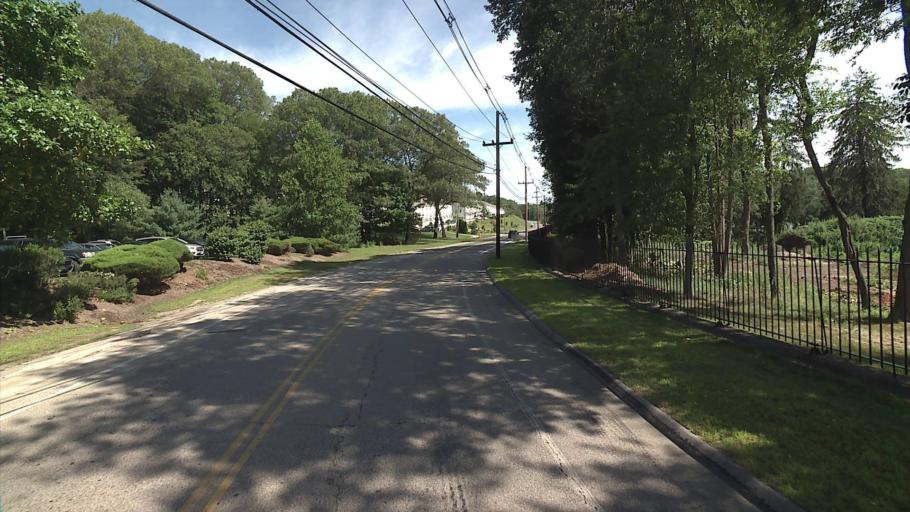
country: US
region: Connecticut
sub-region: New London County
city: Lisbon
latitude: 41.5724
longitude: -72.0485
